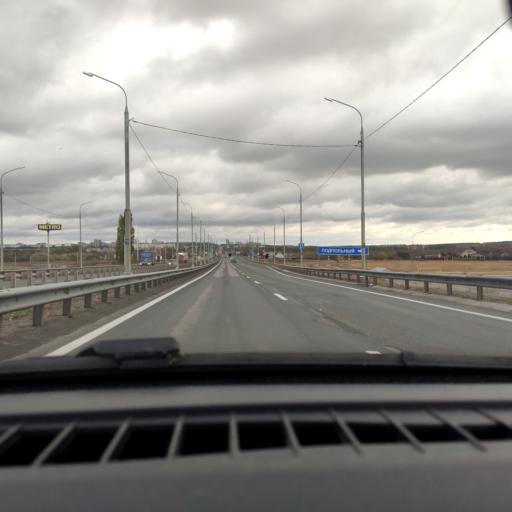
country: RU
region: Voronezj
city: Pridonskoy
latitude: 51.6524
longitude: 39.0591
